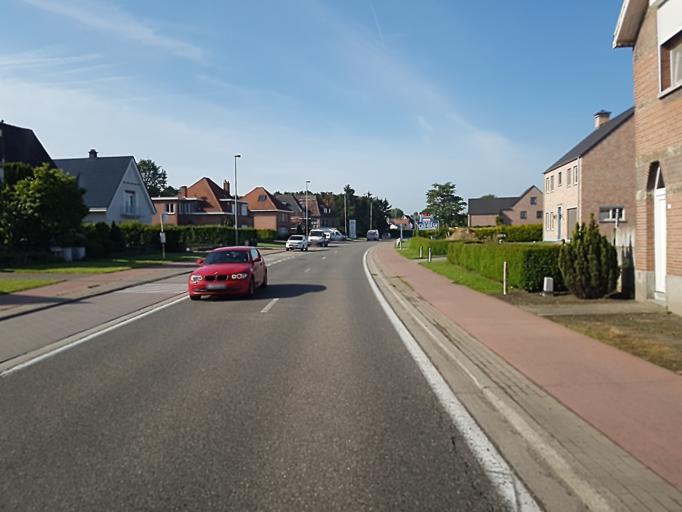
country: BE
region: Flanders
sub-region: Provincie Oost-Vlaanderen
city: Beveren
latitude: 51.2124
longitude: 4.1955
